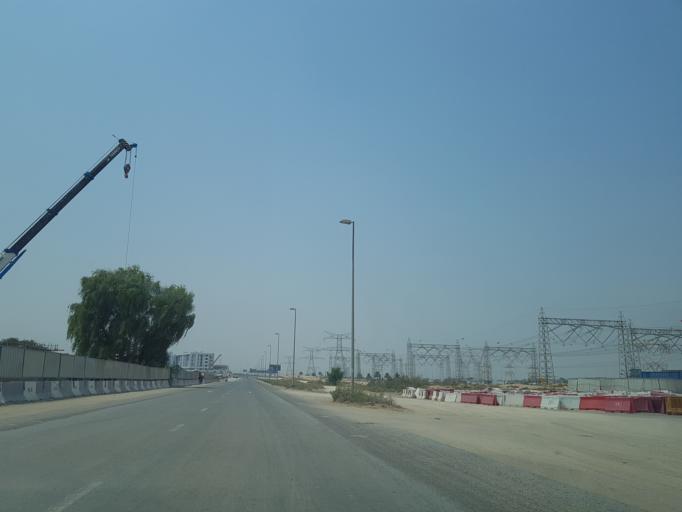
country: AE
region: Ash Shariqah
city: Sharjah
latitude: 25.2263
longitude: 55.4092
